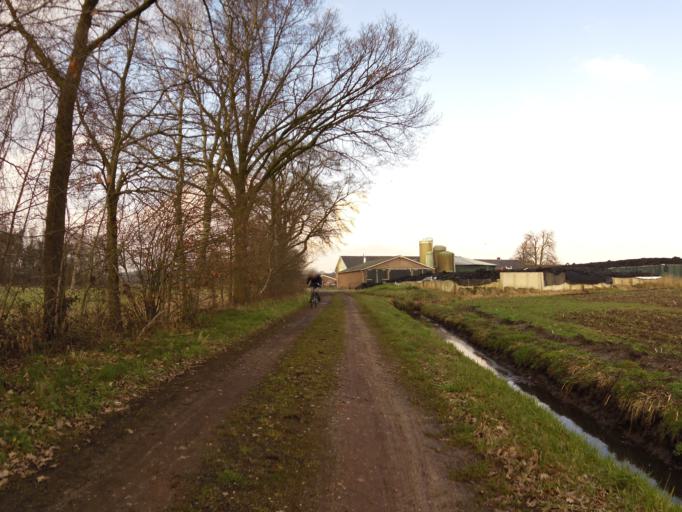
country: NL
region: North Brabant
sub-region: Gemeente Vught
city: Vught
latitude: 51.6226
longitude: 5.3088
